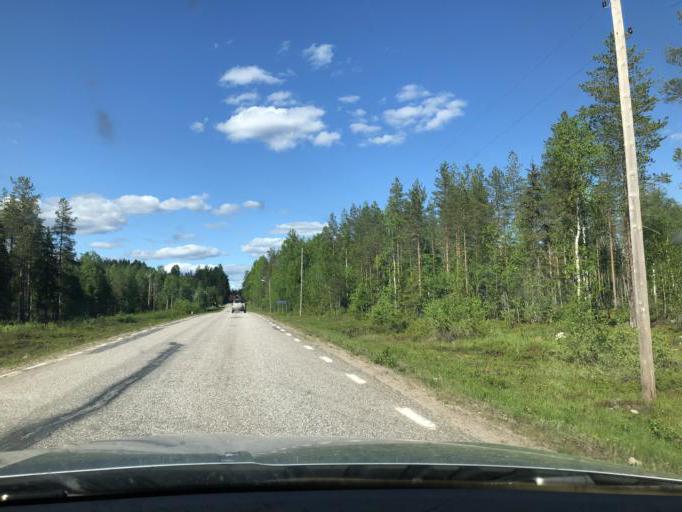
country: SE
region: Norrbotten
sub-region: Kalix Kommun
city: Kalix
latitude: 66.0555
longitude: 23.1920
